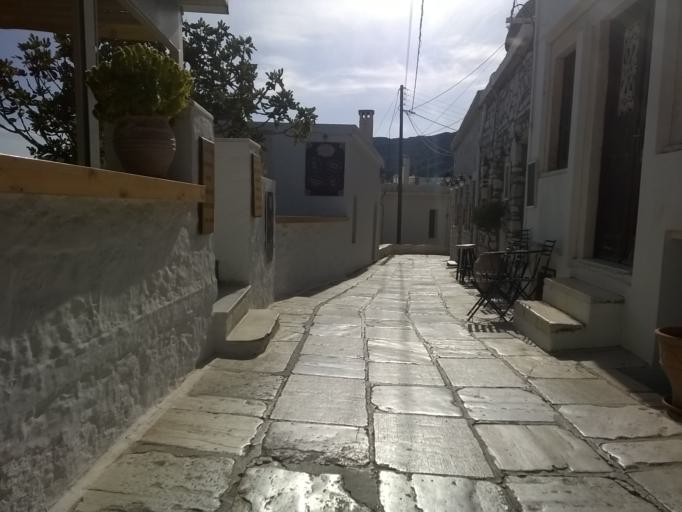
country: GR
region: South Aegean
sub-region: Nomos Kykladon
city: Filotion
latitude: 37.0718
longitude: 25.5211
